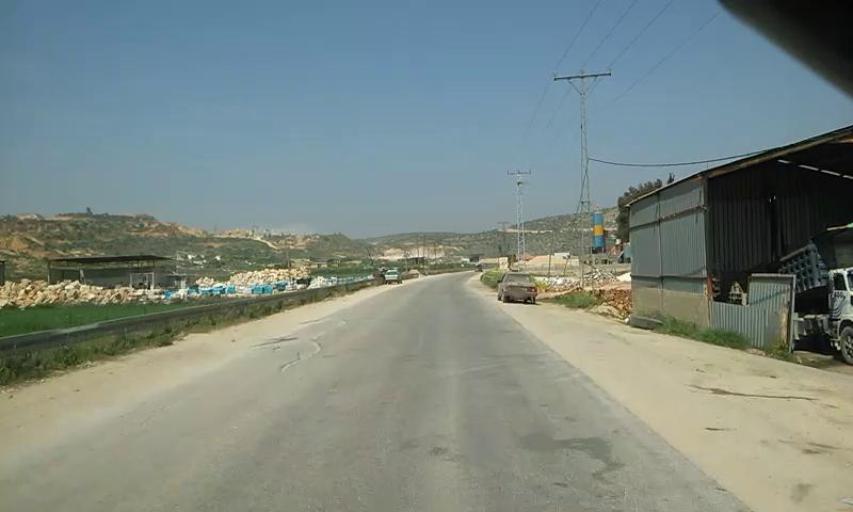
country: PS
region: West Bank
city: Az Zababidah
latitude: 32.3963
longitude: 35.3198
